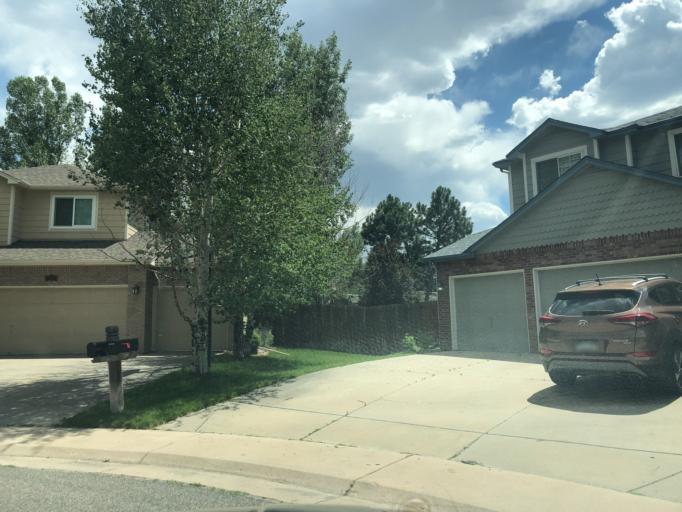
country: US
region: Colorado
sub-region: Arapahoe County
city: Dove Valley
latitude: 39.6220
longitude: -104.7599
